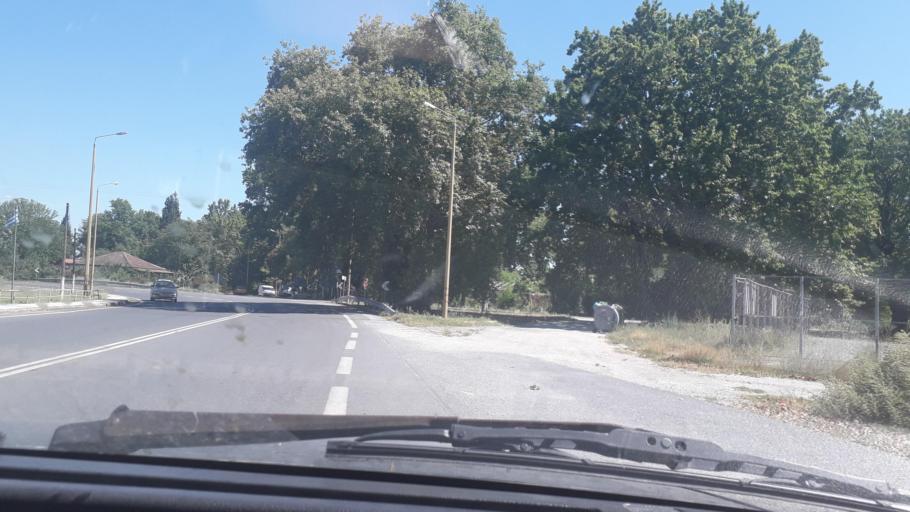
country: GR
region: Central Macedonia
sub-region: Nomos Pellis
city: Tsakoi
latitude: 40.9662
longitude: 22.0250
